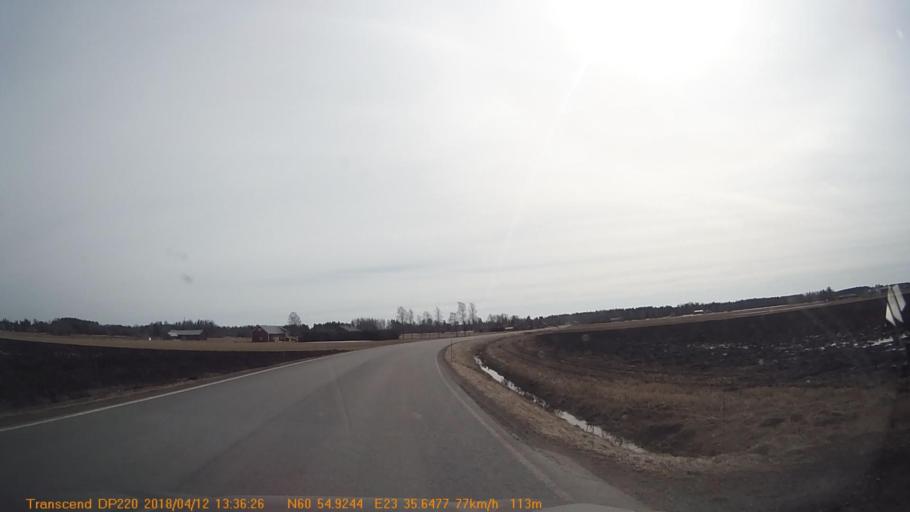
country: FI
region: Haeme
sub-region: Forssa
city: Forssa
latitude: 60.9151
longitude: 23.5944
